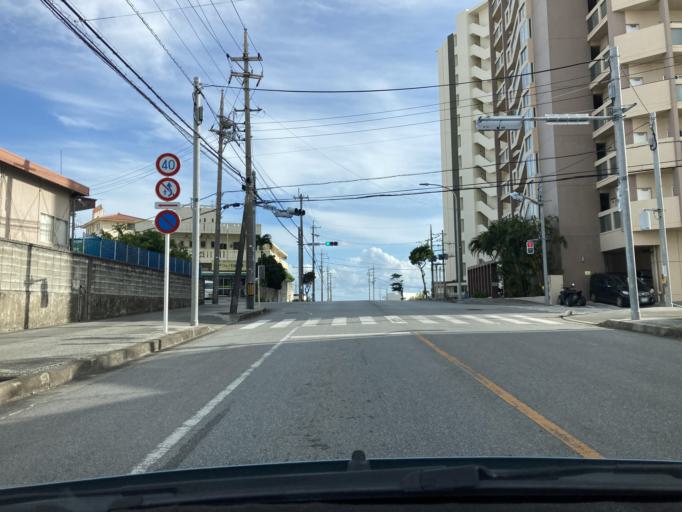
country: JP
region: Okinawa
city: Okinawa
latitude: 26.3398
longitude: 127.8253
